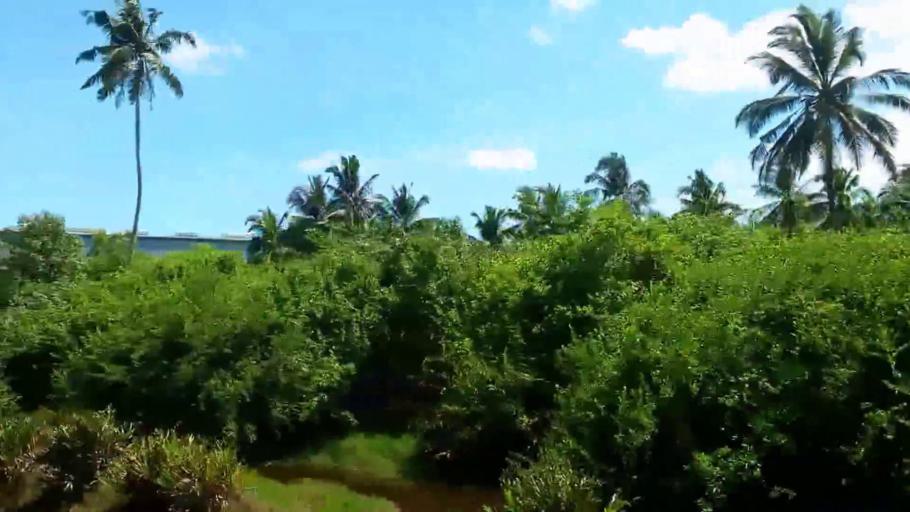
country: LK
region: Southern
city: Hikkaduwa
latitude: 6.1722
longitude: 80.0857
